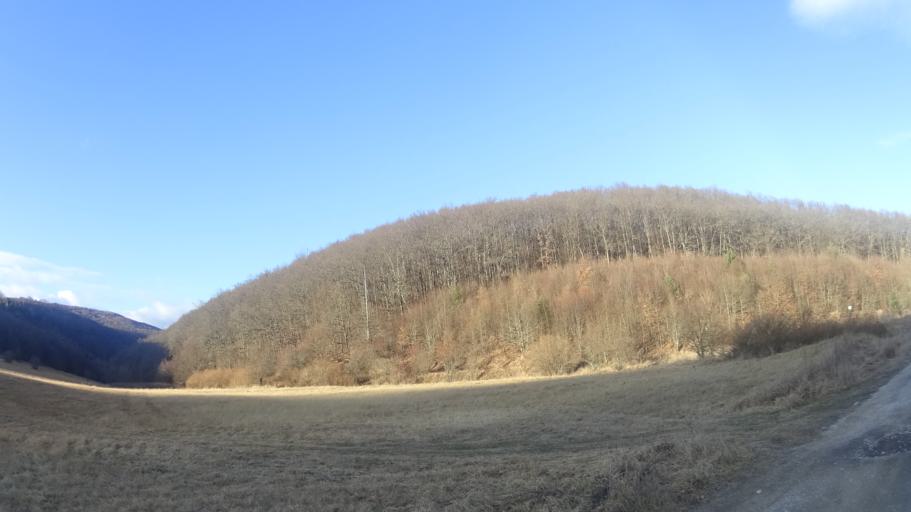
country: HU
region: Borsod-Abauj-Zemplen
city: Bogacs
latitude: 48.0302
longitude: 20.5513
